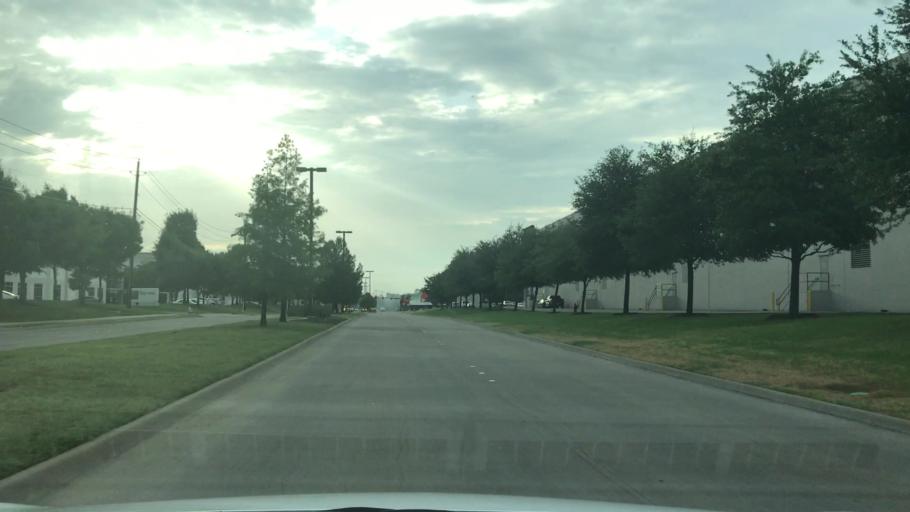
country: US
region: Texas
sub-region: Dallas County
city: Coppell
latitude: 32.9547
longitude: -97.0146
